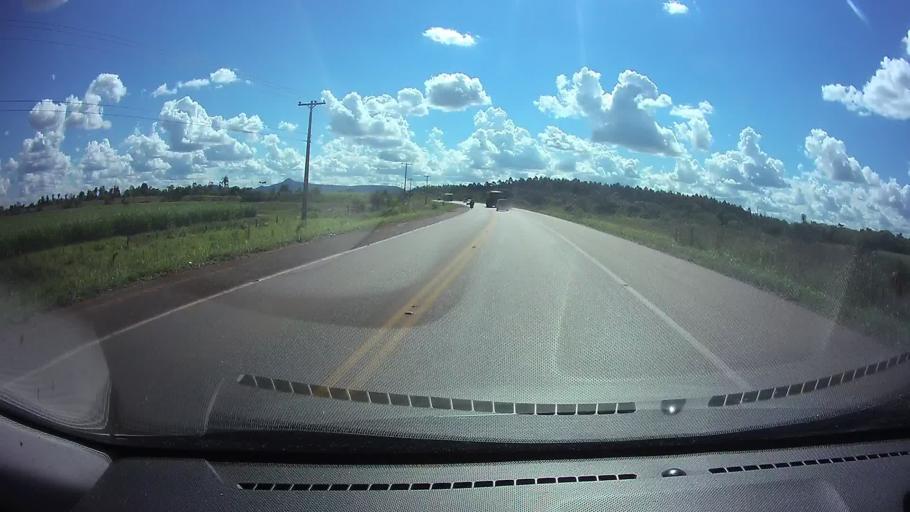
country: PY
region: Guaira
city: Coronel Martinez
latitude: -25.7584
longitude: -56.7051
